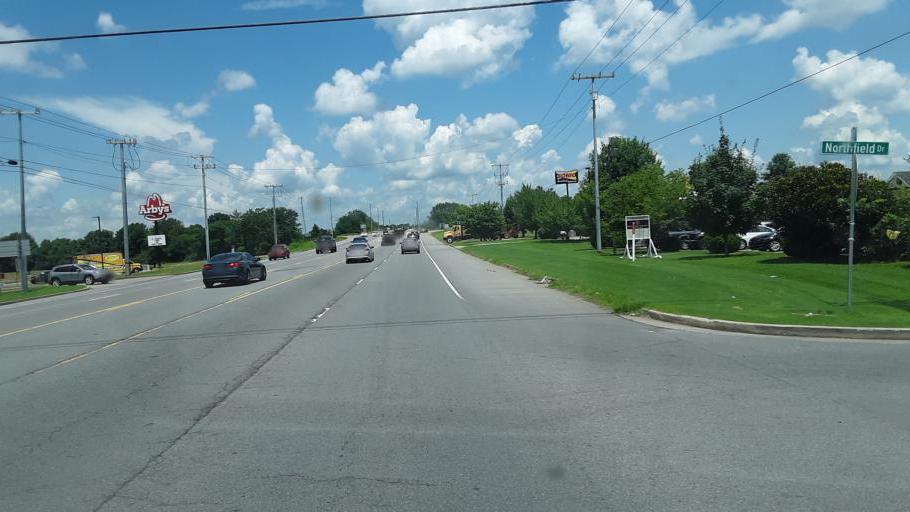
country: US
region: Tennessee
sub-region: Montgomery County
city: Clarksville
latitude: 36.6257
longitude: -87.3176
